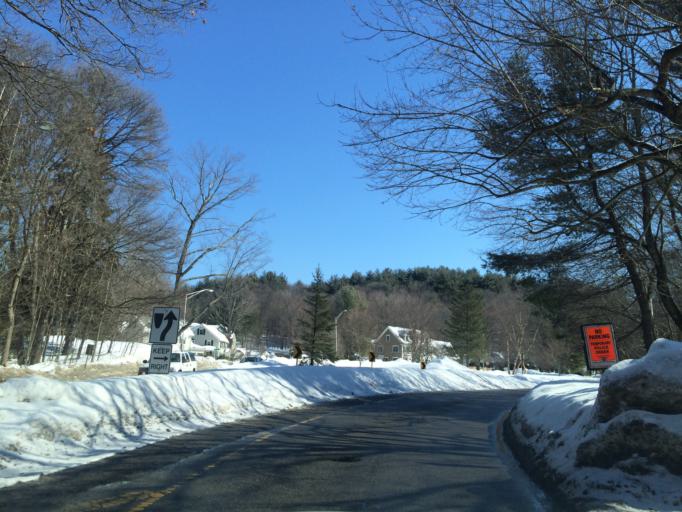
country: US
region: Massachusetts
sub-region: Norfolk County
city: Wellesley
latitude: 42.2987
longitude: -71.2803
